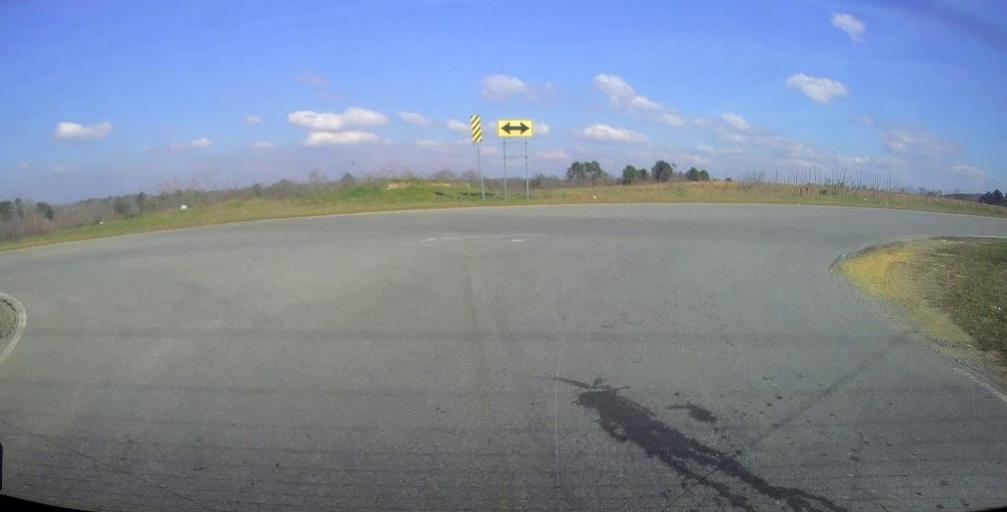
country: US
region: Georgia
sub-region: Wilkinson County
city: Gordon
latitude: 32.8968
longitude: -83.3019
